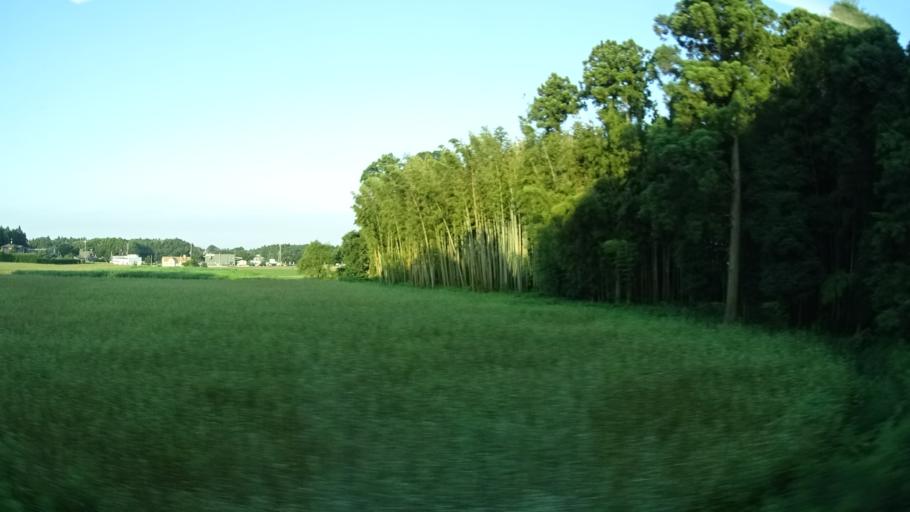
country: JP
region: Ibaraki
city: Naka
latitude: 36.0153
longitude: 140.1604
